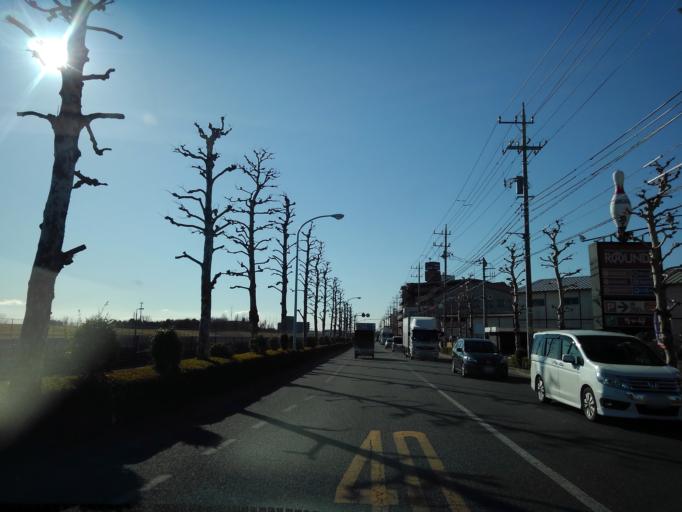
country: JP
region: Tokyo
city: Fussa
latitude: 35.7355
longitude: 139.3830
